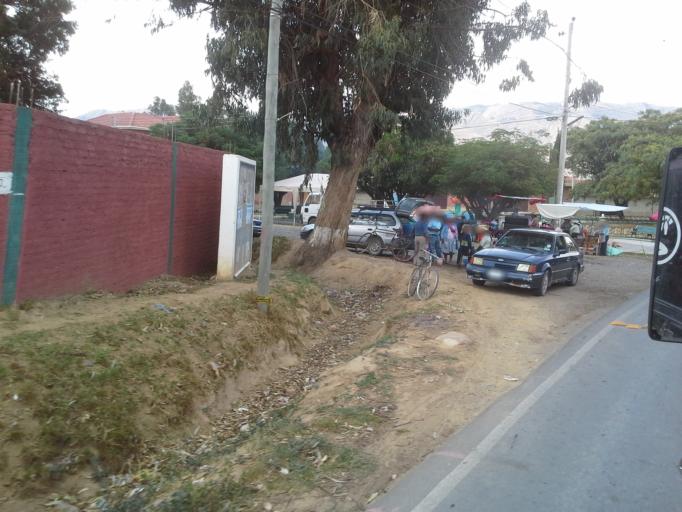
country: BO
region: Cochabamba
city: Tarata
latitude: -17.5635
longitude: -66.0096
